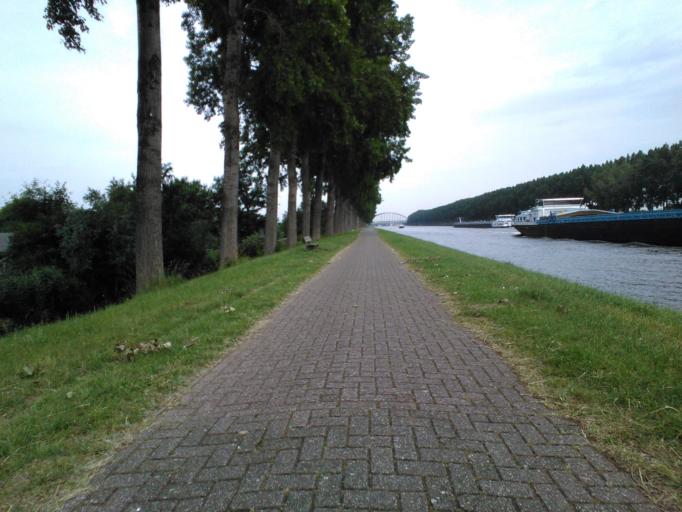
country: NL
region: North Holland
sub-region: Gemeente Amsterdam
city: Driemond
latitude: 52.3118
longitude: 5.0189
